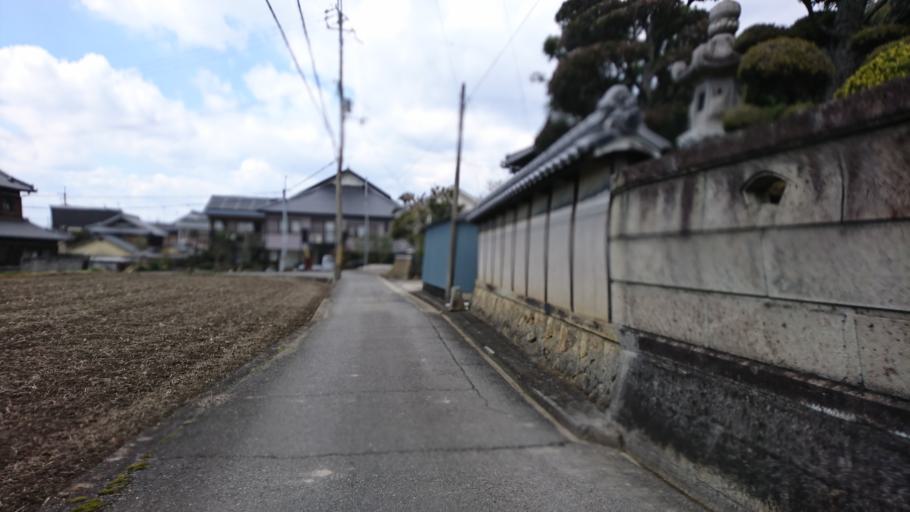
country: JP
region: Hyogo
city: Miki
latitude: 34.7687
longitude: 134.9526
